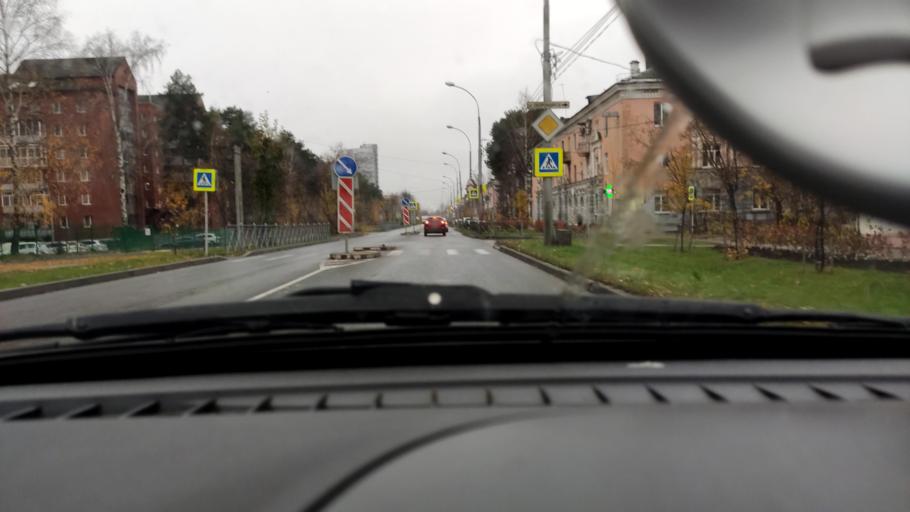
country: RU
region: Perm
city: Kultayevo
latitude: 58.0030
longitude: 55.9622
